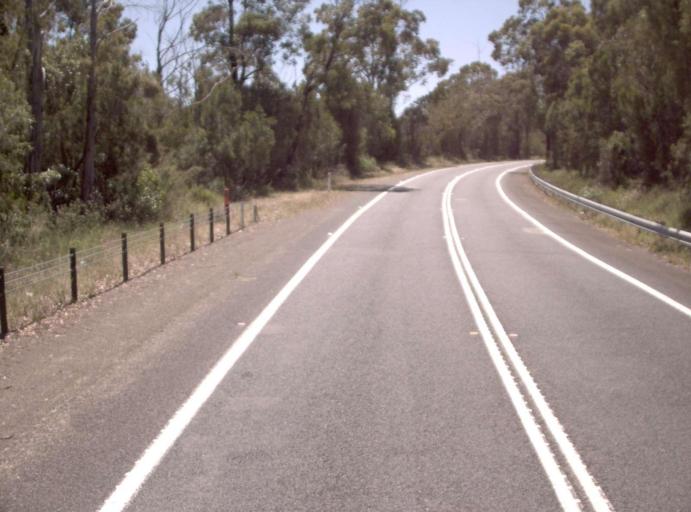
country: AU
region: Victoria
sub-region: East Gippsland
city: Lakes Entrance
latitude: -37.8313
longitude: 148.0310
